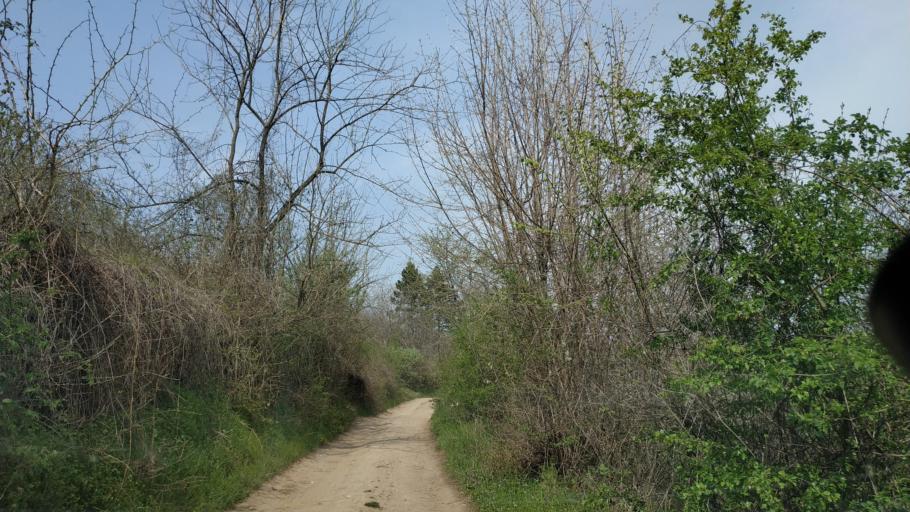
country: RS
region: Central Serbia
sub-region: Nisavski Okrug
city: Aleksinac
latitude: 43.5402
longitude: 21.7262
